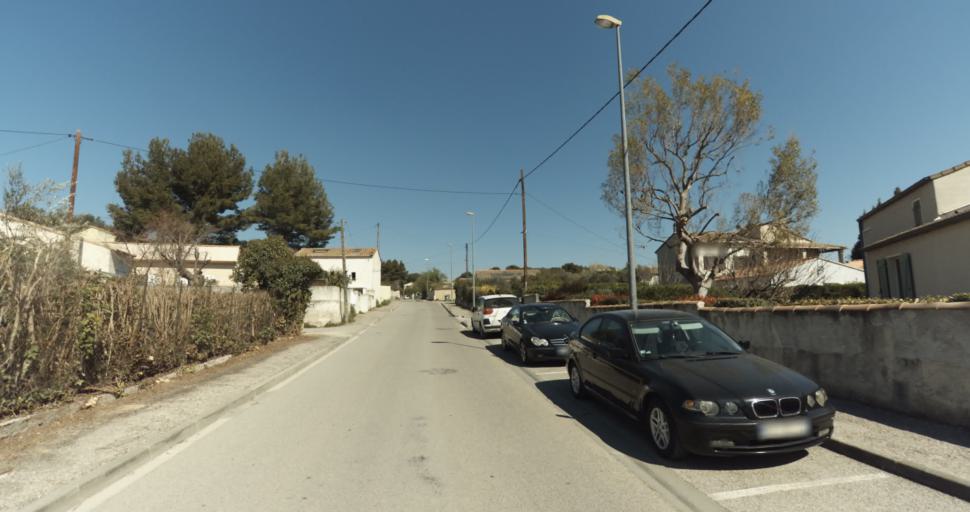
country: FR
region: Provence-Alpes-Cote d'Azur
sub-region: Departement des Bouches-du-Rhone
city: Pelissanne
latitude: 43.6356
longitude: 5.1589
